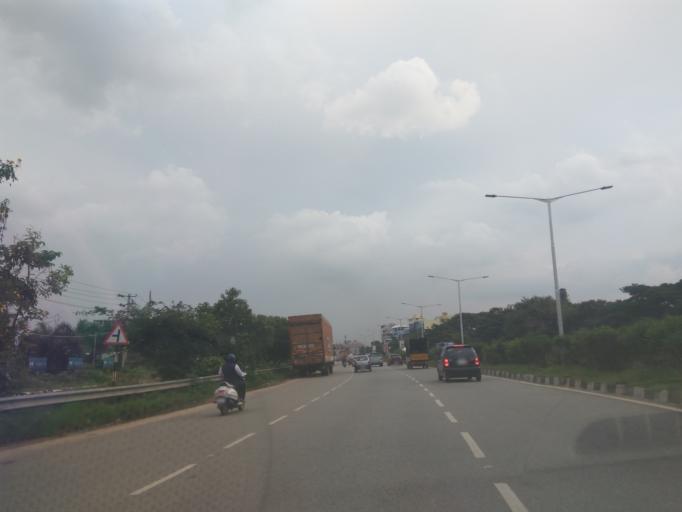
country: IN
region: Karnataka
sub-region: Bangalore Rural
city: Hoskote
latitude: 13.0150
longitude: 77.7008
